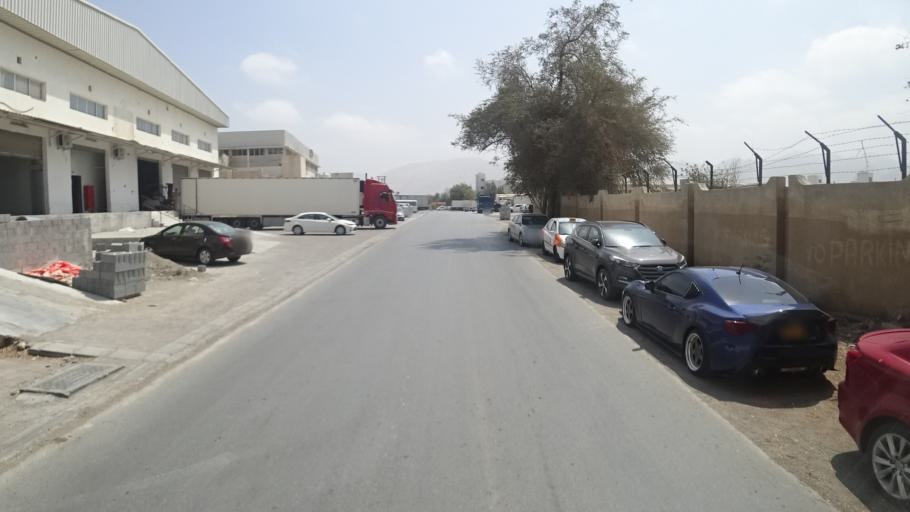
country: OM
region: Muhafazat Masqat
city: Bawshar
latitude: 23.5776
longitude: 58.3702
